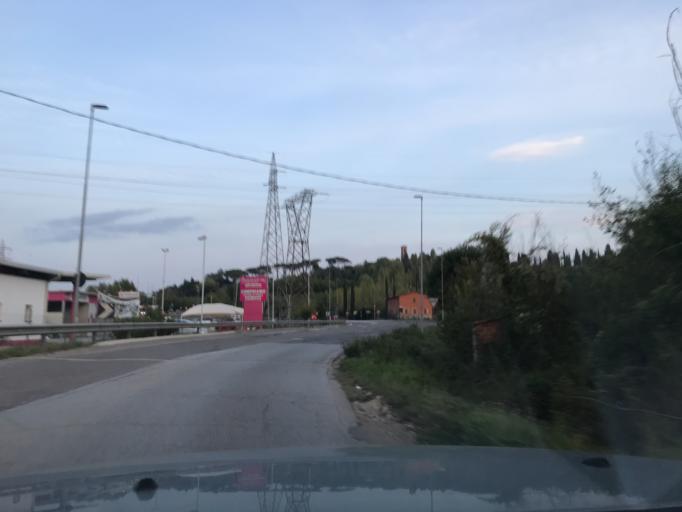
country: IT
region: Umbria
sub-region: Provincia di Perugia
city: Via Lippia
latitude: 43.0872
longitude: 12.4656
